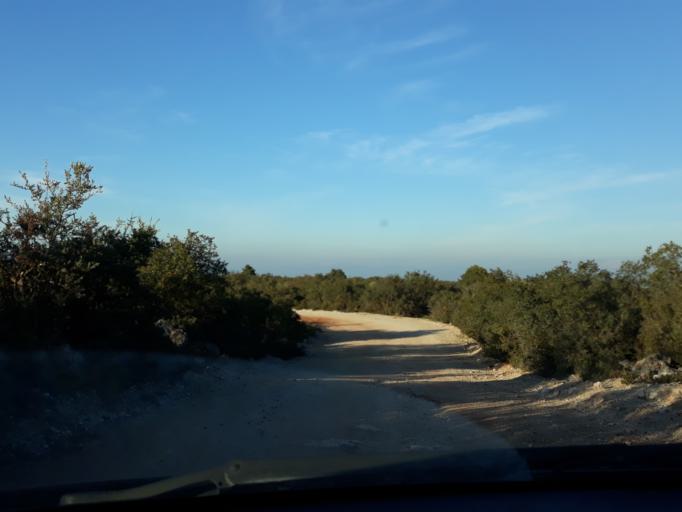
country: GR
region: Central Greece
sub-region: Nomos Voiotias
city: Ayios Thomas
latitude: 38.2435
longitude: 23.5344
